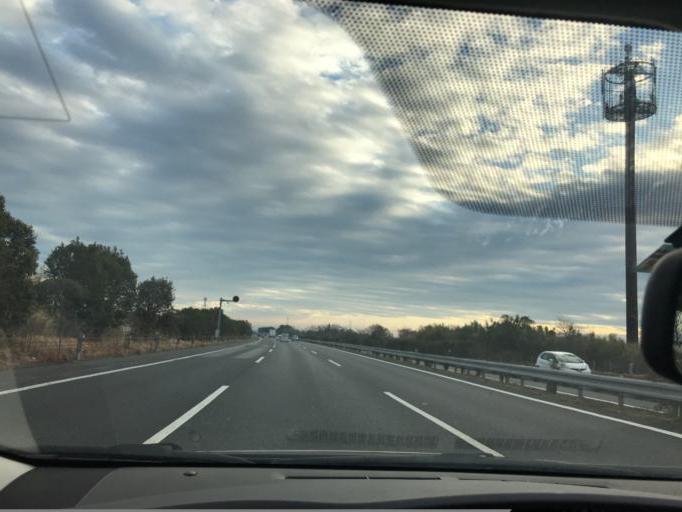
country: JP
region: Ibaraki
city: Mitsukaido
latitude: 35.9811
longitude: 140.0060
